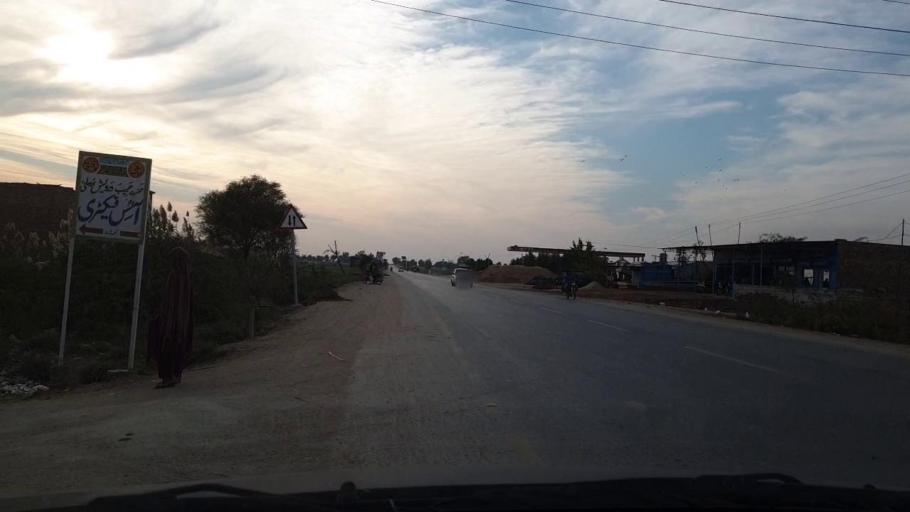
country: PK
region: Sindh
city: Khadro
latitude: 26.1523
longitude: 68.7148
